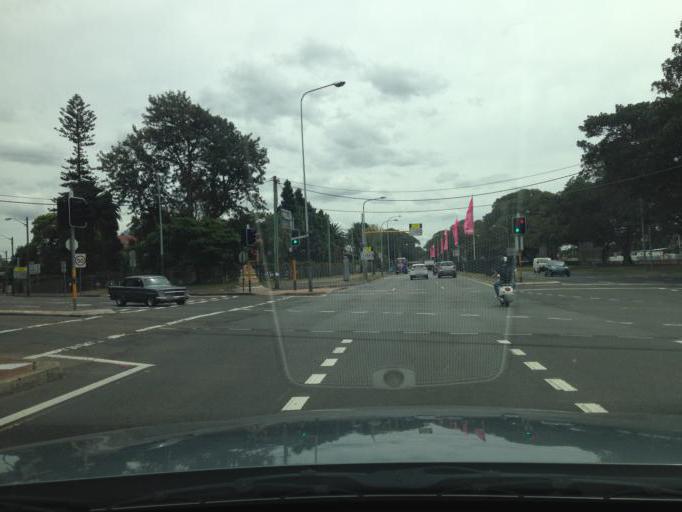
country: AU
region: New South Wales
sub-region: Woollahra
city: Paddington
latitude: -33.8954
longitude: 151.2215
